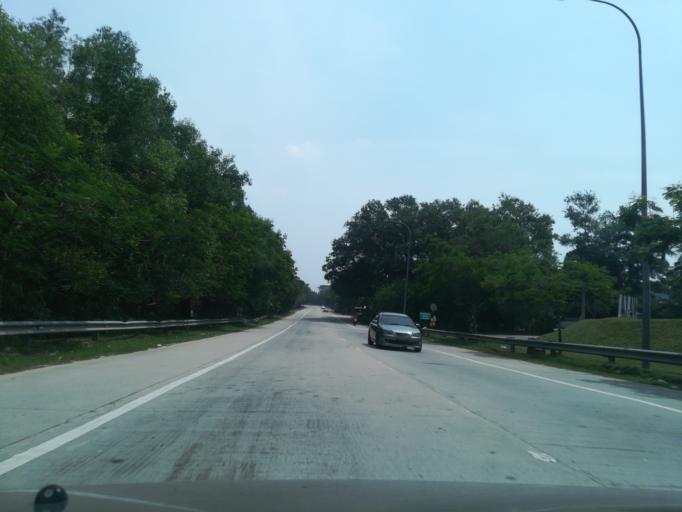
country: MY
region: Kedah
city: Kulim
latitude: 5.4203
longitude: 100.5667
